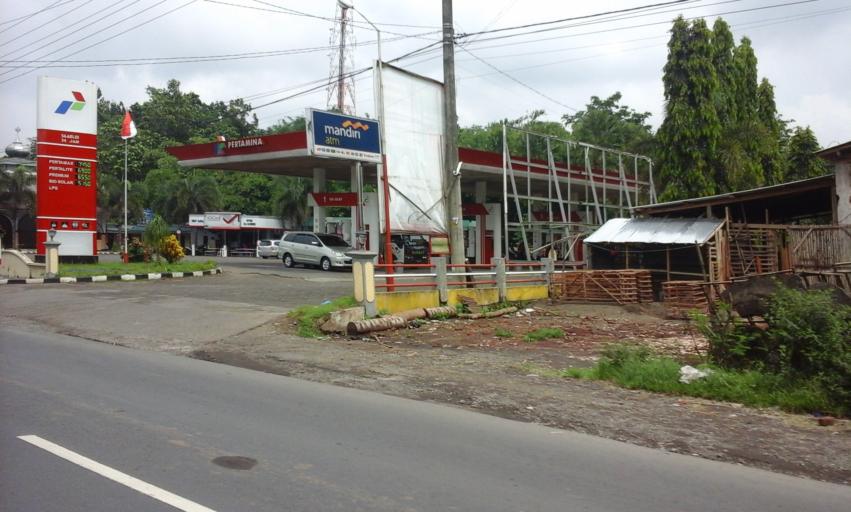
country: ID
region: East Java
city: Klatakan
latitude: -8.1903
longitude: 113.4971
